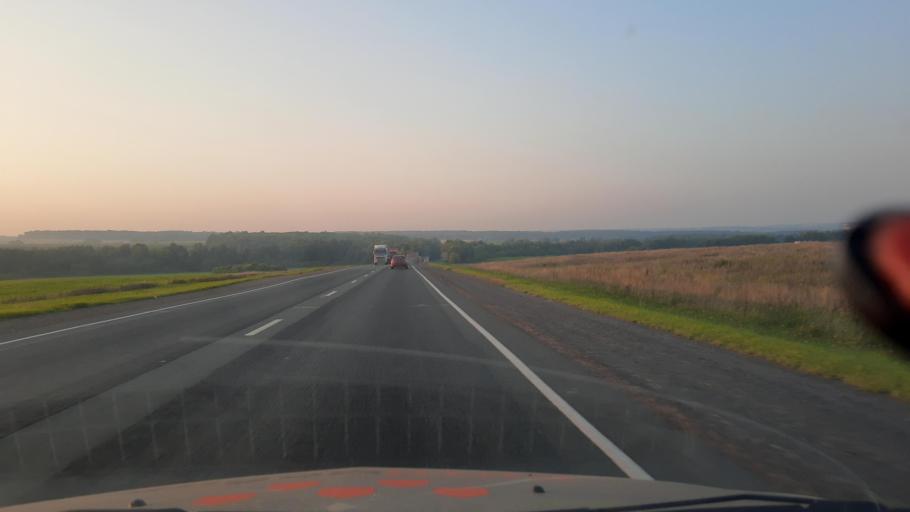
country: RU
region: Bashkortostan
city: Avdon
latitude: 54.7550
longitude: 55.7807
